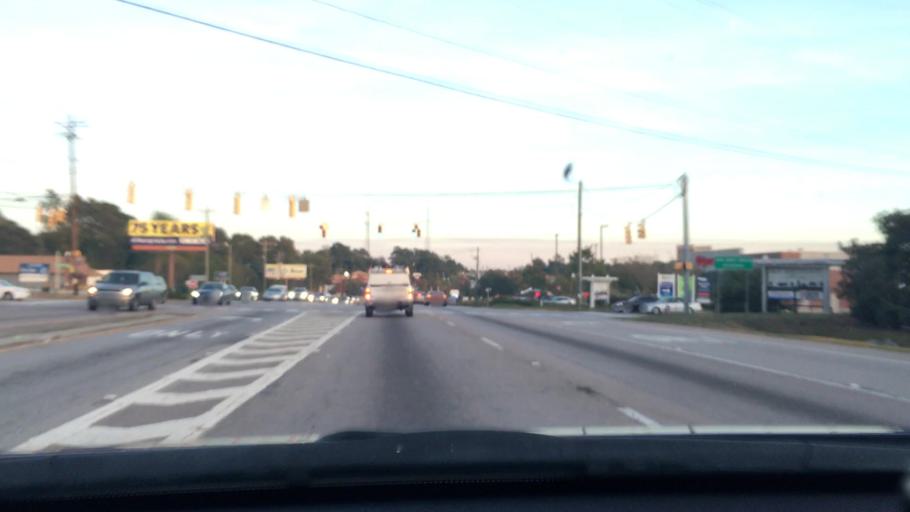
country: US
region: South Carolina
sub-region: Richland County
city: Hopkins
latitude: 33.9565
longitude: -80.9310
